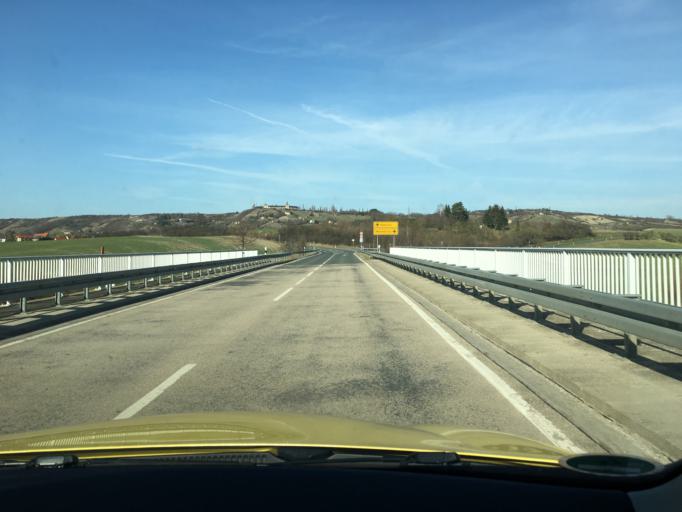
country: DE
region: Saxony-Anhalt
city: Laucha
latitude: 51.2279
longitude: 11.6796
